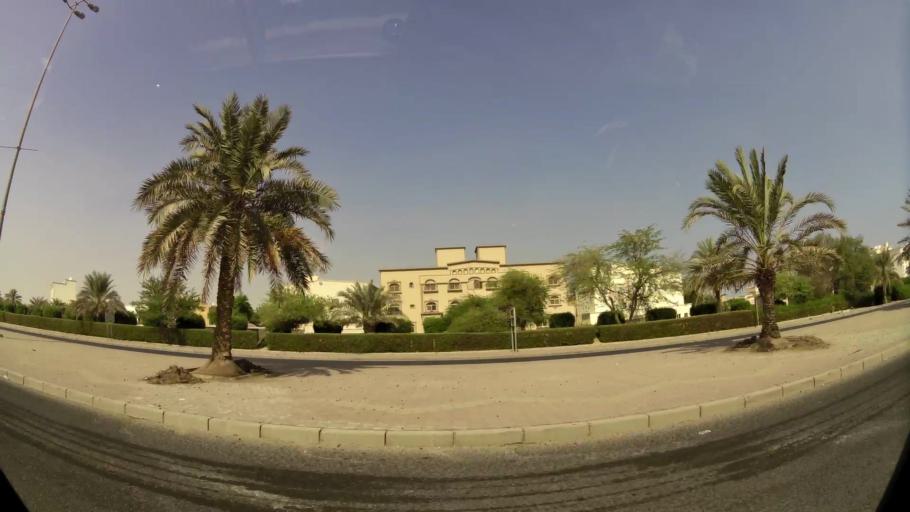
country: KW
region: Al Ahmadi
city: Al Fahahil
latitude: 29.0916
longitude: 48.1096
